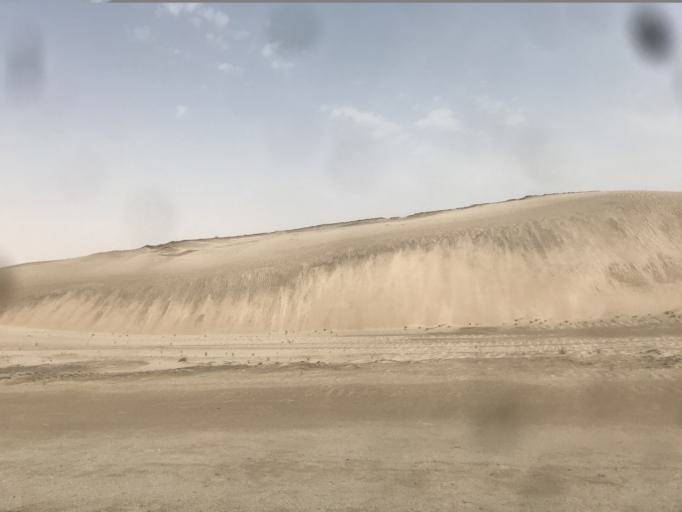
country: SA
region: Eastern Province
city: Abqaiq
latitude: 25.9060
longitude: 50.0079
